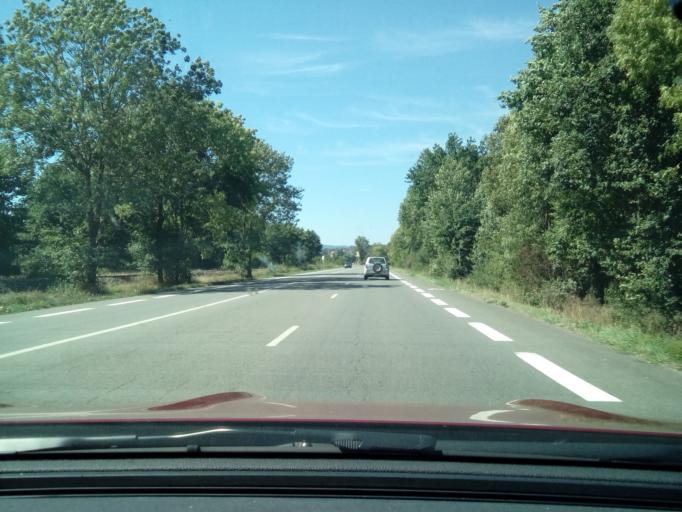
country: FR
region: Rhone-Alpes
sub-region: Departement du Rhone
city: Chessy
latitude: 45.8784
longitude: 4.6403
